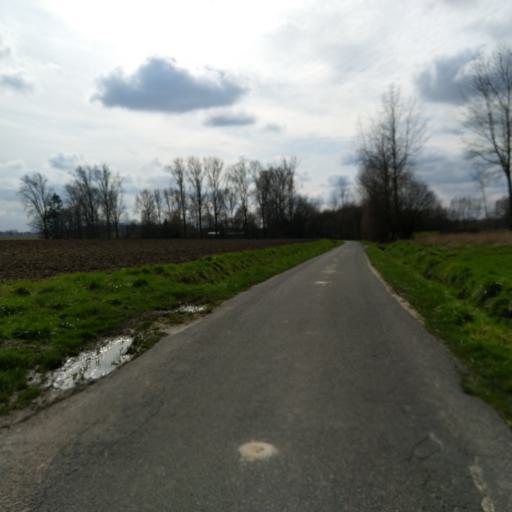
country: BE
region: Wallonia
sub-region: Province du Hainaut
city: Soignies
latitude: 50.5357
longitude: 4.0576
